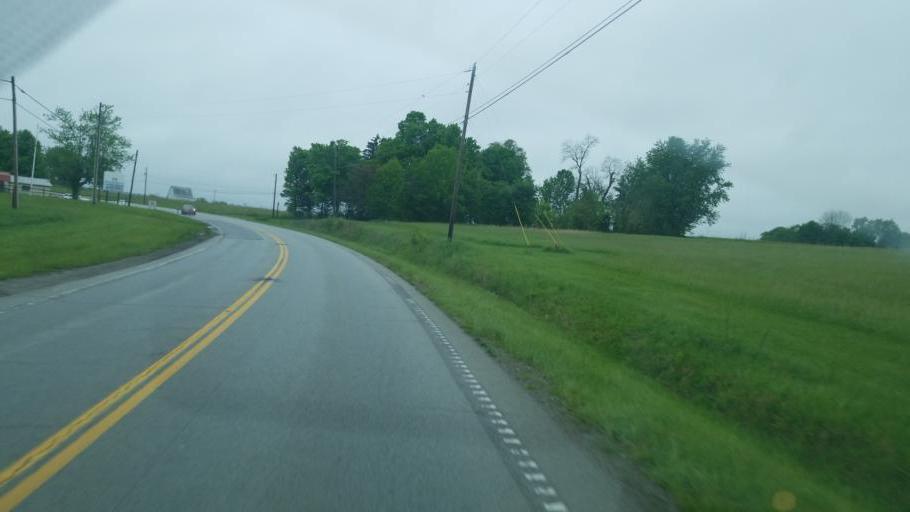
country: US
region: Ohio
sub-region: Highland County
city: Hillsboro
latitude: 39.2486
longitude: -83.6056
